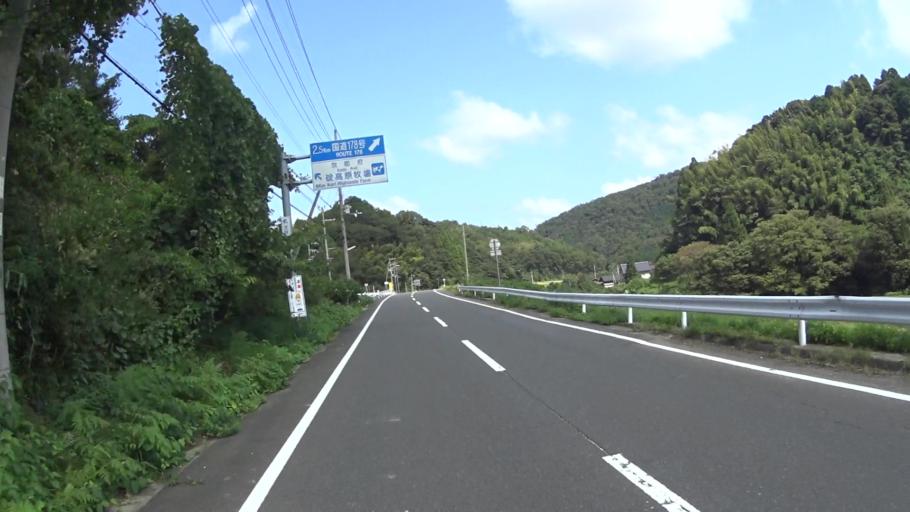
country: JP
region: Kyoto
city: Miyazu
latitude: 35.7024
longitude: 135.2500
